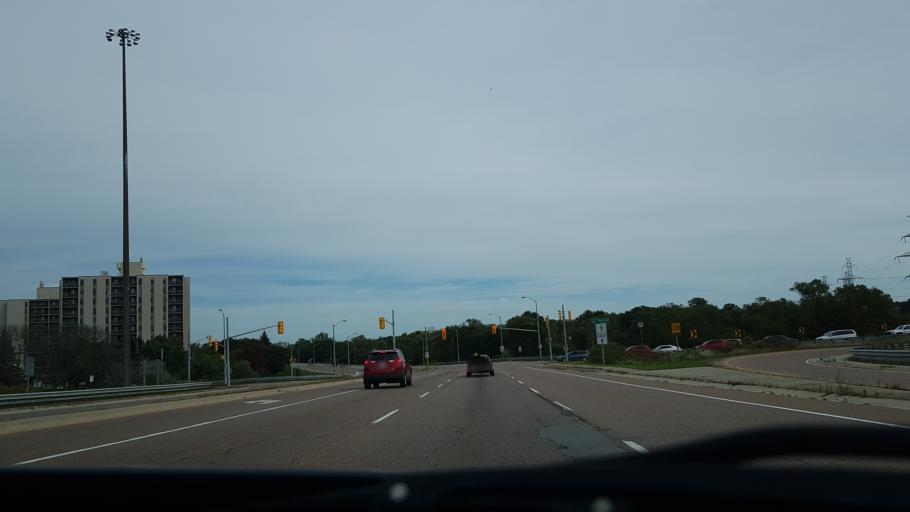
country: CA
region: Ontario
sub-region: Wellington County
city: Guelph
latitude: 43.5279
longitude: -80.2627
